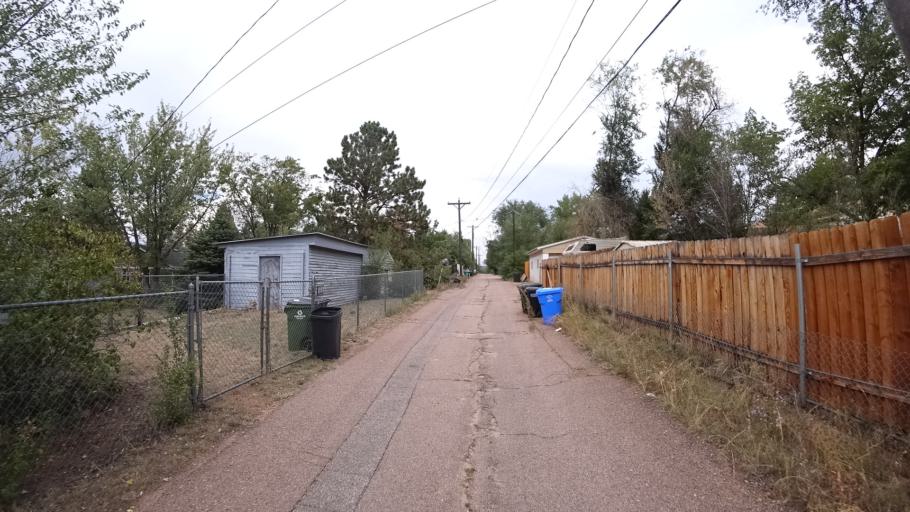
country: US
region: Colorado
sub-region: El Paso County
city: Colorado Springs
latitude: 38.8629
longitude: -104.7935
